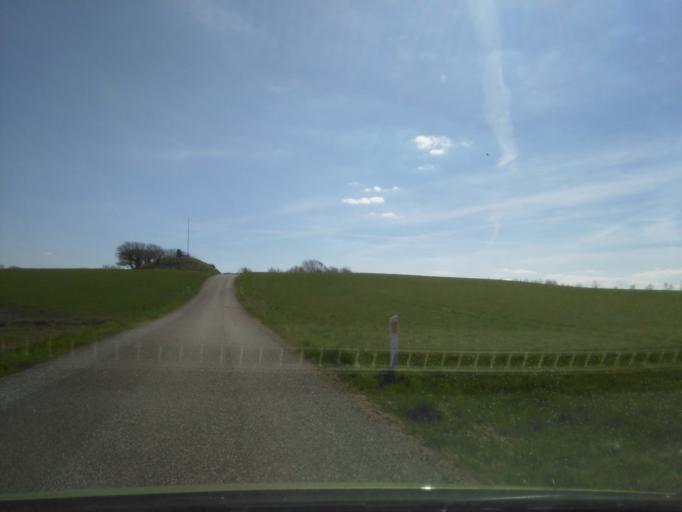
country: DK
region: Central Jutland
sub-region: Viborg Kommune
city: Viborg
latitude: 56.3546
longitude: 9.3388
